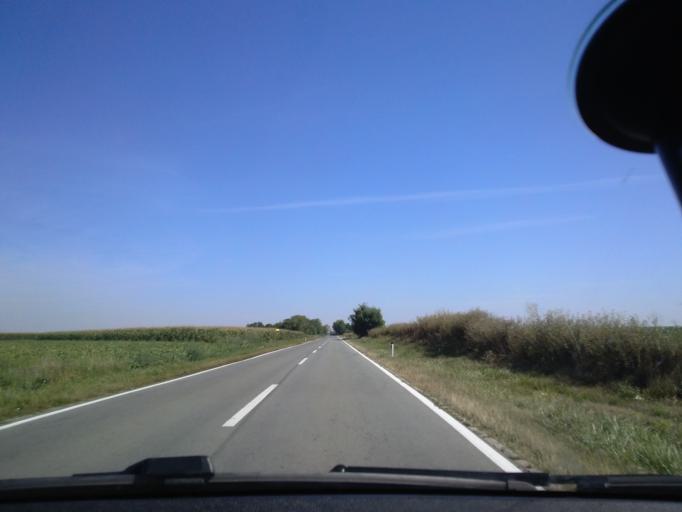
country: RS
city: Doroslovo
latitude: 45.6397
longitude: 19.1986
